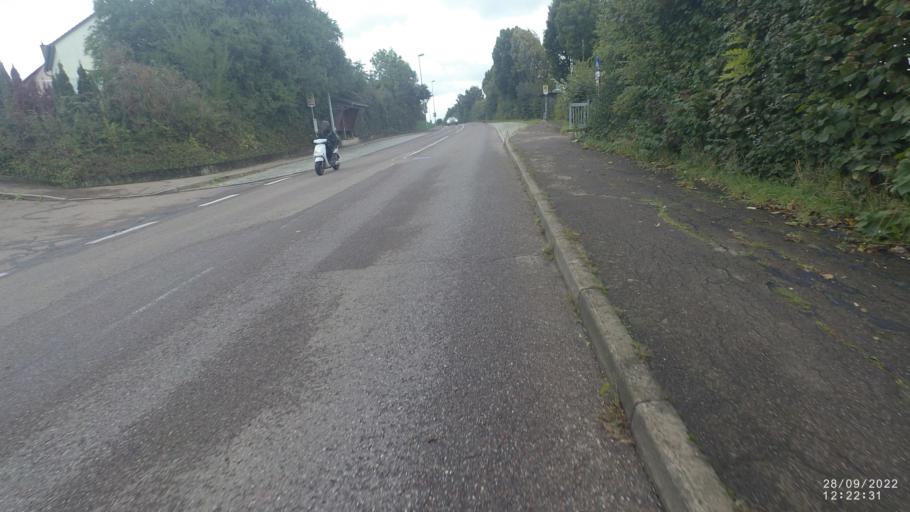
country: DE
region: Baden-Wuerttemberg
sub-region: Regierungsbezirk Stuttgart
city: Wangen
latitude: 48.7222
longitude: 9.6082
